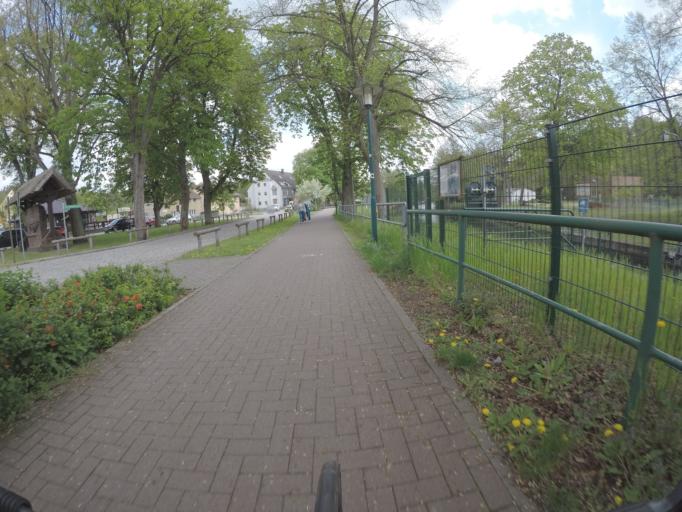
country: DE
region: Brandenburg
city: Marienwerder
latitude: 52.8919
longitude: 13.6388
